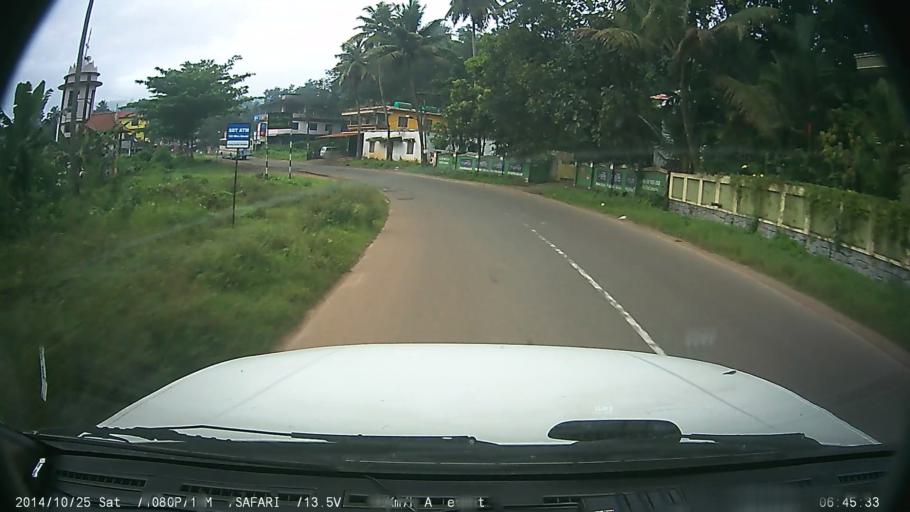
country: IN
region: Kerala
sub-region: Ernakulam
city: Muvattupuzha
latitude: 9.9470
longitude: 76.5743
